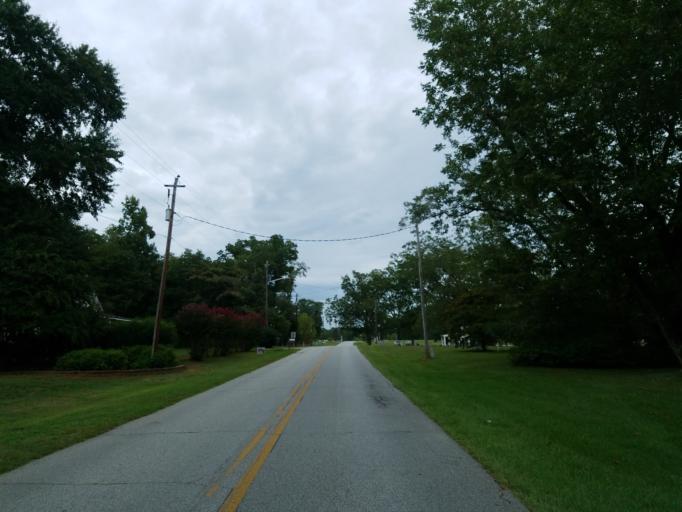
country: US
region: Georgia
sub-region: Lamar County
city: Barnesville
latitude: 33.1152
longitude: -84.2001
